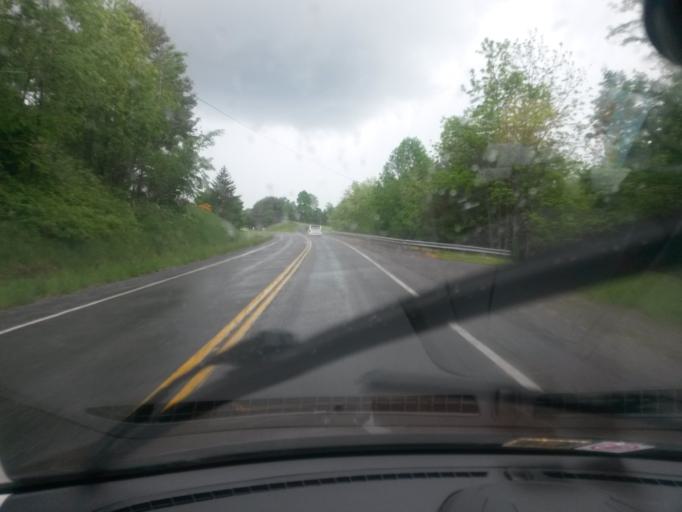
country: US
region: Virginia
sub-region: Floyd County
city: Floyd
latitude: 36.9692
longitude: -80.3837
